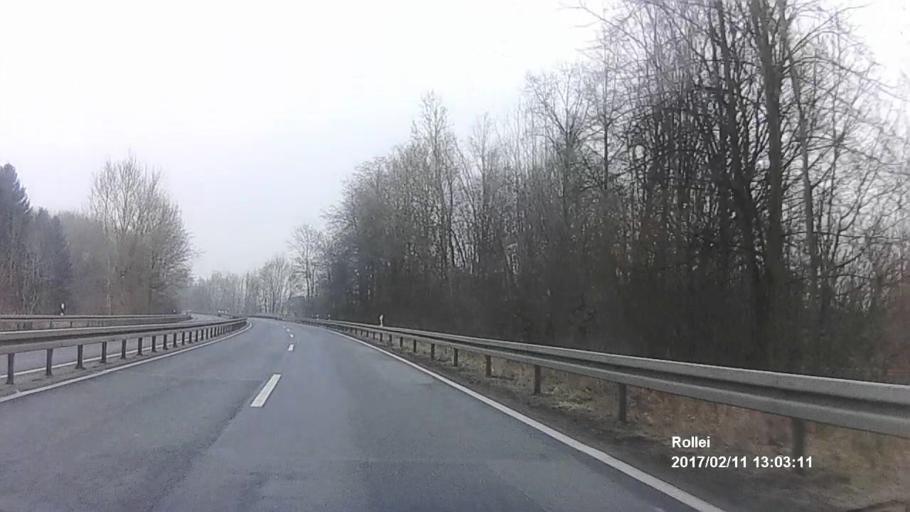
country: DE
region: Lower Saxony
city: Windhausen
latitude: 51.7836
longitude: 10.1996
